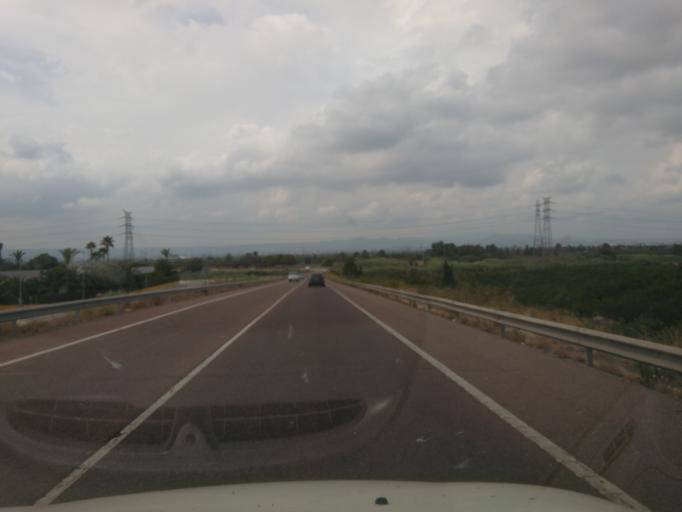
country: ES
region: Valencia
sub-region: Provincia de Valencia
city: Alzira
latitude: 39.1610
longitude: -0.4507
